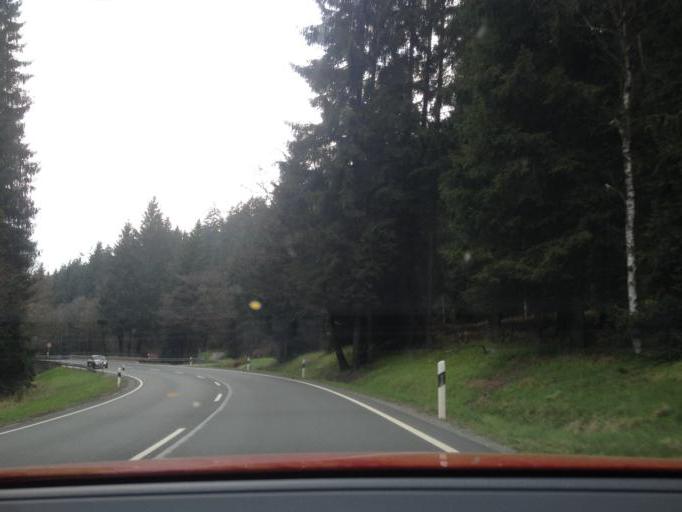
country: DE
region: Bavaria
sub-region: Upper Franconia
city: Bischofsgrun
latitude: 50.0606
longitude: 11.7858
